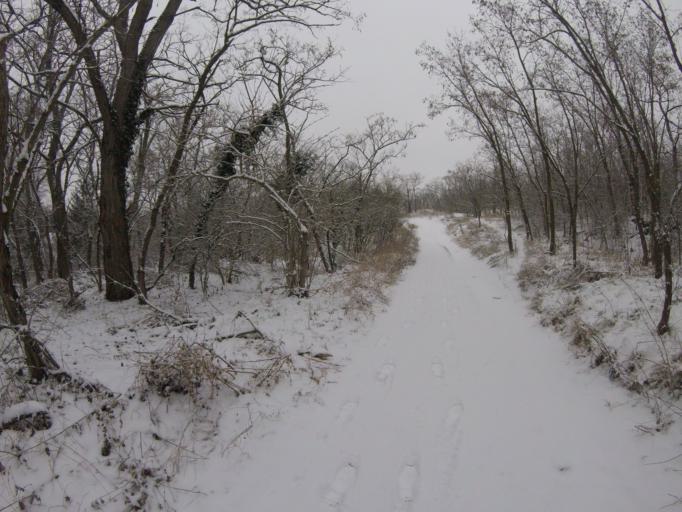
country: HU
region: Fejer
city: Pakozd
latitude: 47.2236
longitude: 18.5330
